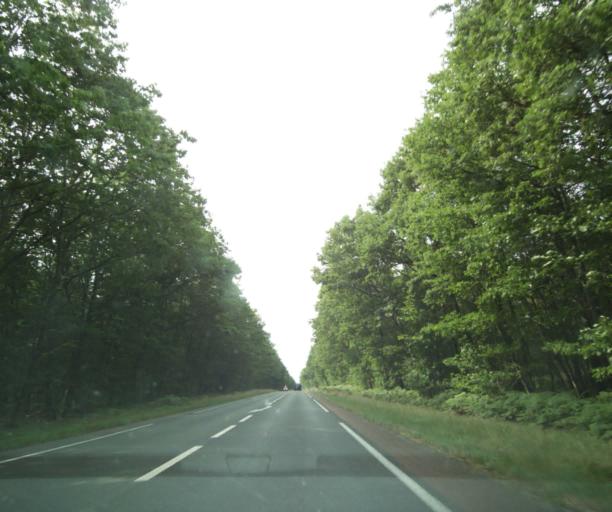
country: FR
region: Pays de la Loire
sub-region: Departement de la Sarthe
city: Marigne-Laille
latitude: 47.7651
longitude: 0.3531
